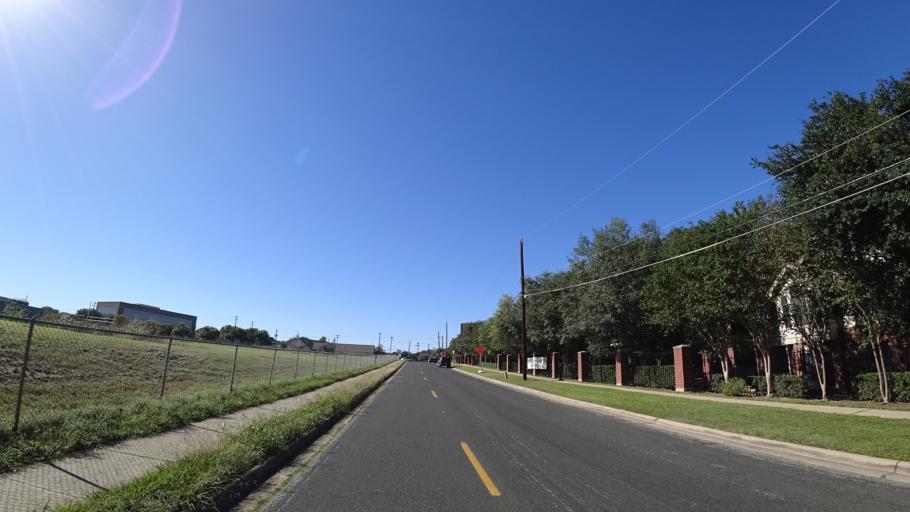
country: US
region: Texas
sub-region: Travis County
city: Rollingwood
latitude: 30.2375
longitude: -97.7872
